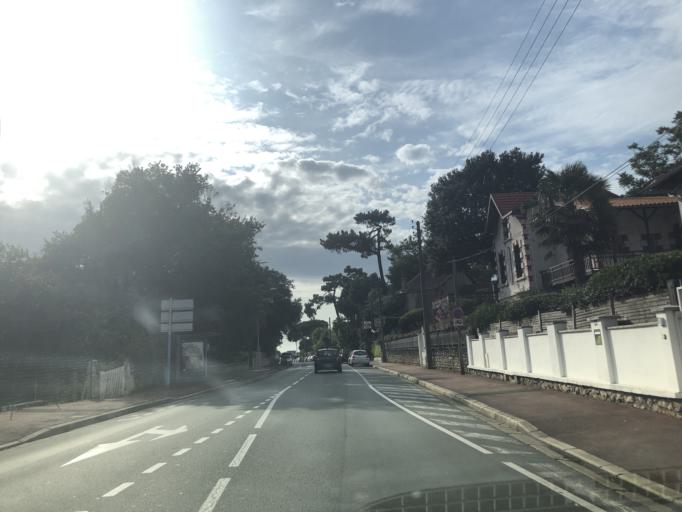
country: FR
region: Poitou-Charentes
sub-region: Departement de la Charente-Maritime
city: Royan
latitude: 45.6245
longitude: -1.0458
